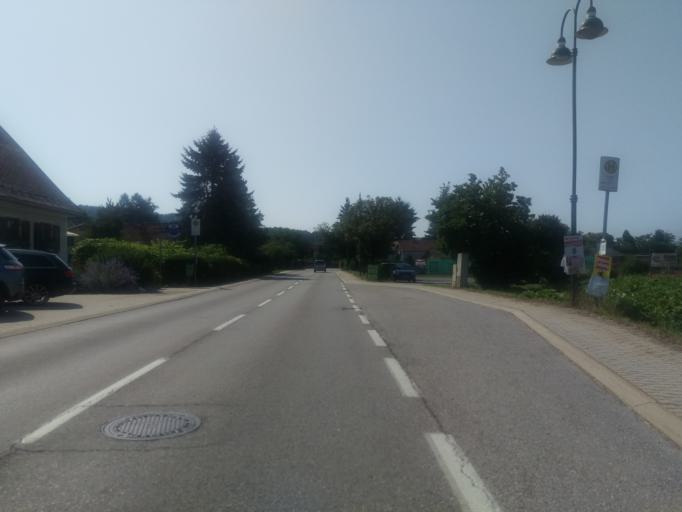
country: AT
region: Styria
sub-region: Politischer Bezirk Graz-Umgebung
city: Fernitz
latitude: 46.9683
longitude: 15.5023
